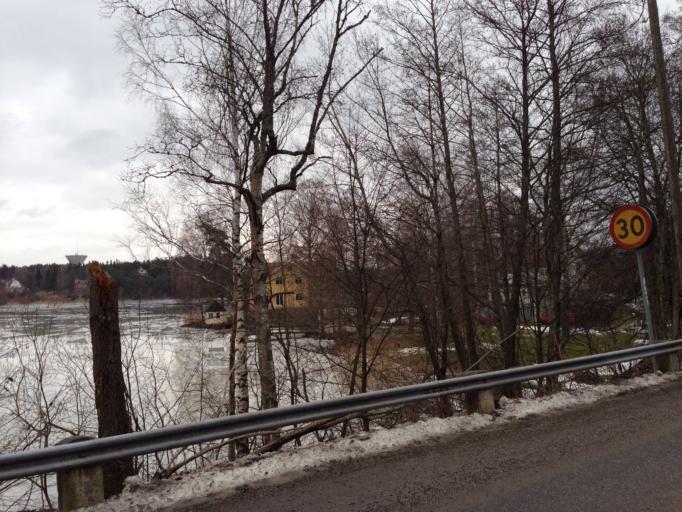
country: SE
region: Stockholm
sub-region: Salems Kommun
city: Ronninge
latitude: 59.1938
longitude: 17.7338
